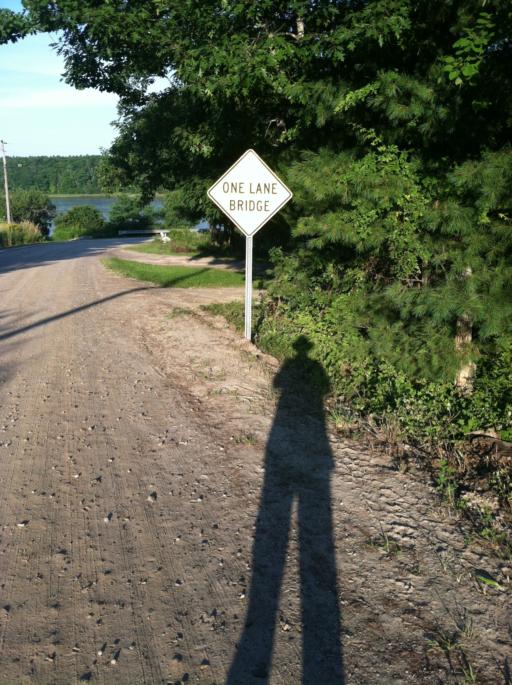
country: US
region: Maine
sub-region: Cumberland County
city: Freeport
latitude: 43.8286
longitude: -70.0748
